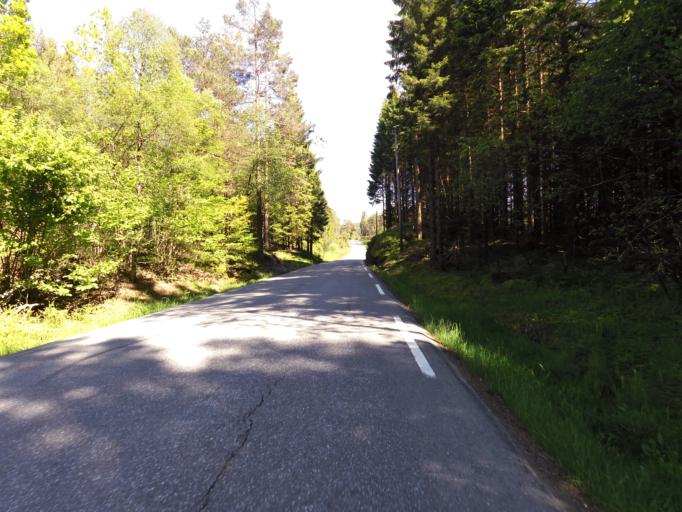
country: NO
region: Hordaland
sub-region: Stord
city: Sagvag
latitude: 59.7895
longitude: 5.4392
